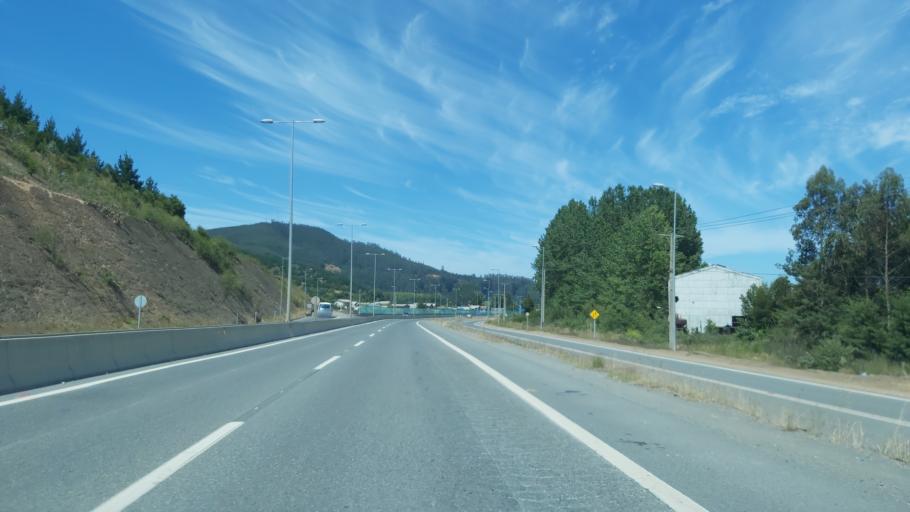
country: CL
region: Biobio
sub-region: Provincia de Concepcion
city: Lota
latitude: -37.1068
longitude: -73.1408
